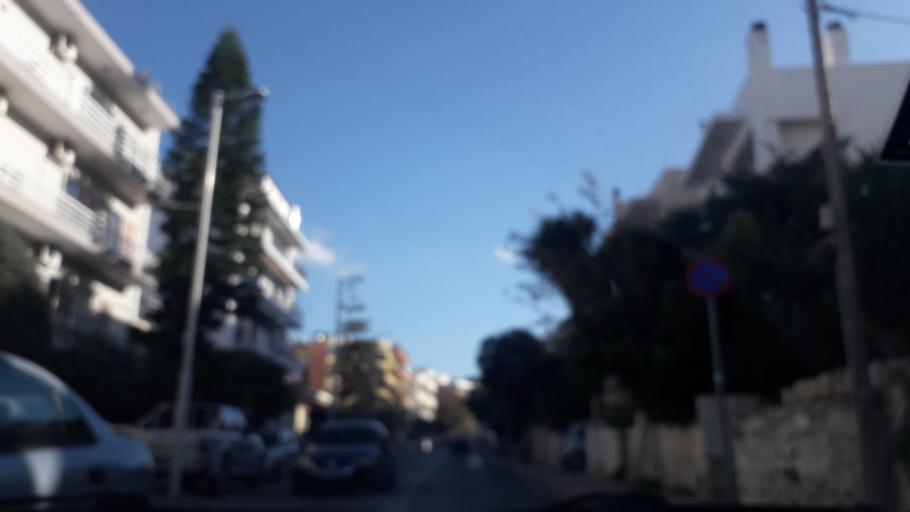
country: GR
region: Crete
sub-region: Nomos Rethymnis
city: Rethymno
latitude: 35.3646
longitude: 24.4710
